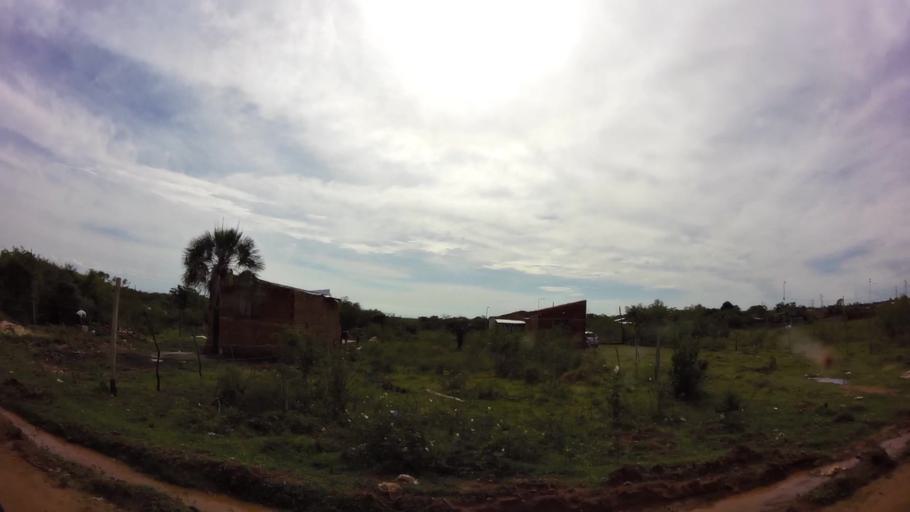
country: PY
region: Central
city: Limpio
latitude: -25.1210
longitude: -57.4819
